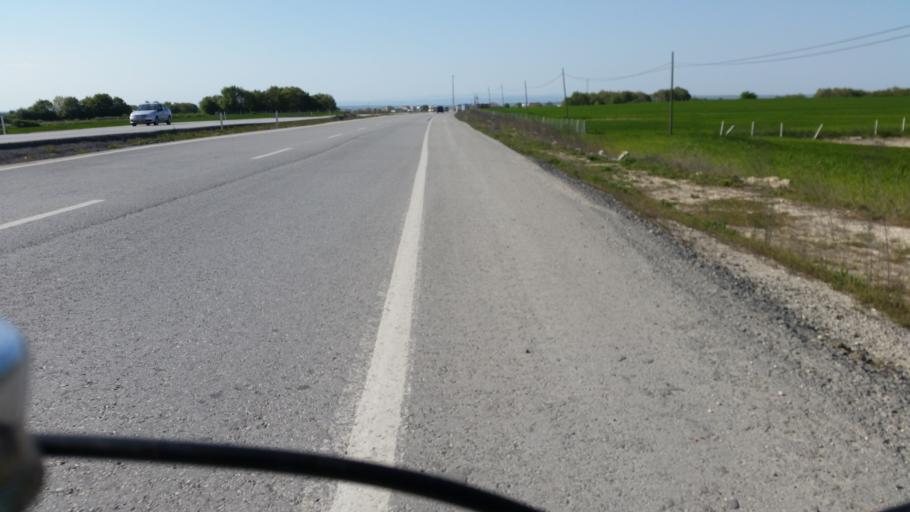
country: TR
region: Tekirdag
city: Cerkezkoey
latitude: 41.3449
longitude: 27.9619
